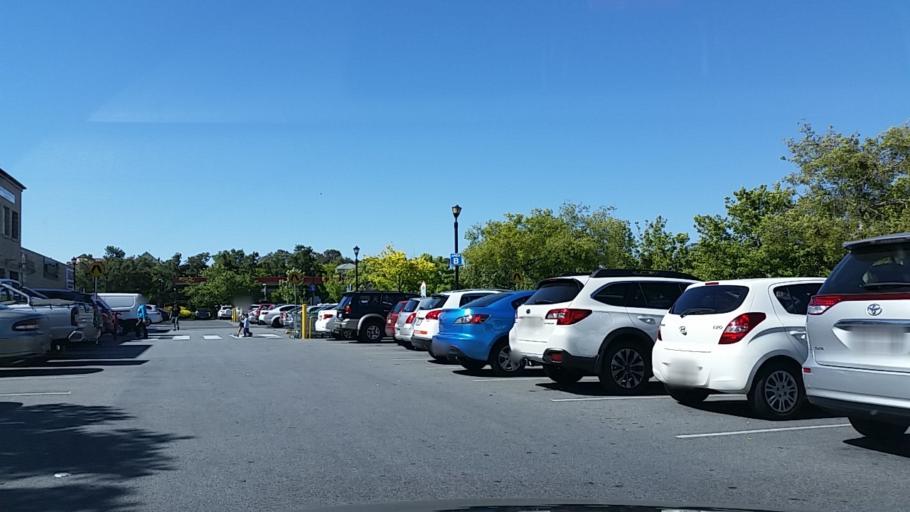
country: AU
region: South Australia
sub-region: Tea Tree Gully
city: Golden Grove
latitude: -34.7904
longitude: 138.6952
